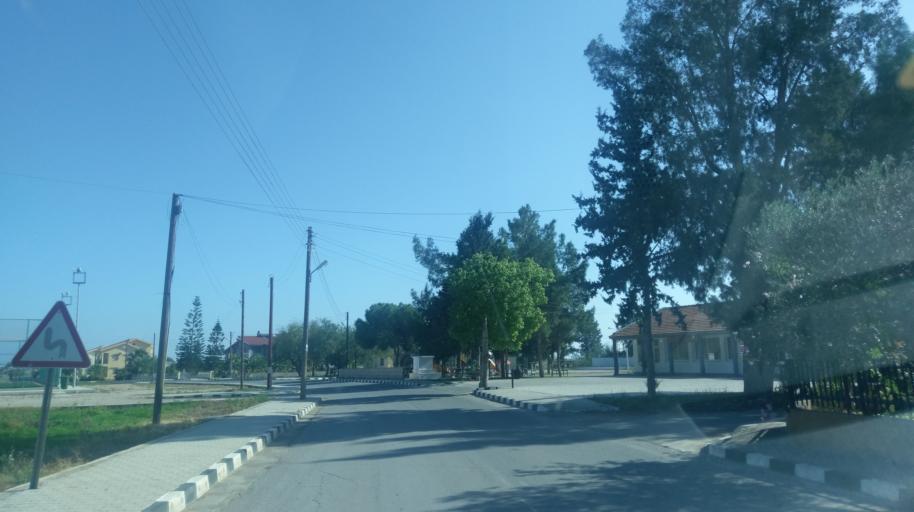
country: CY
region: Ammochostos
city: Trikomo
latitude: 35.2368
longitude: 33.8633
